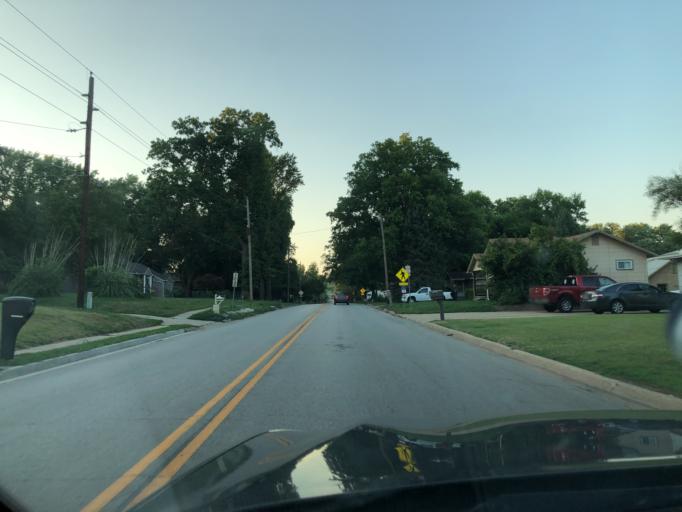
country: US
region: Kansas
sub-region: Leavenworth County
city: Leavenworth
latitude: 39.3196
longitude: -94.9506
